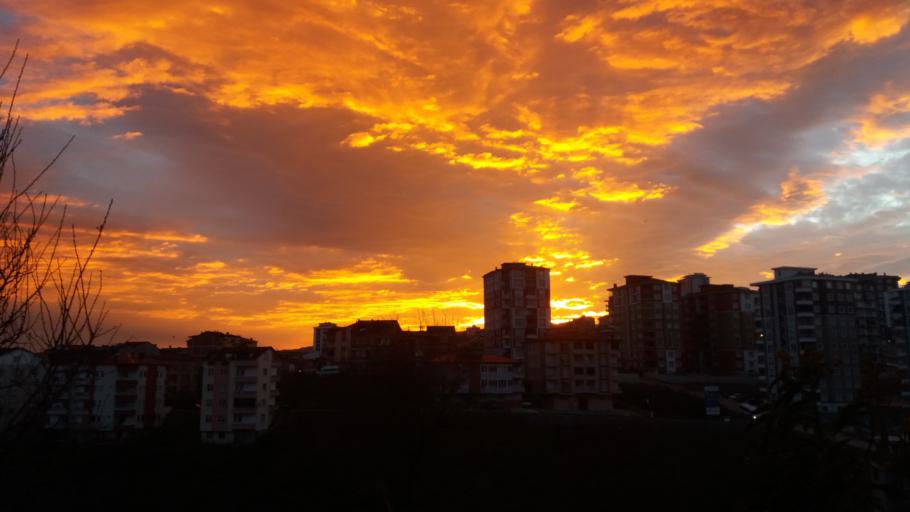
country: TR
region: Ordu
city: Ordu
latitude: 40.9744
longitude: 37.8758
